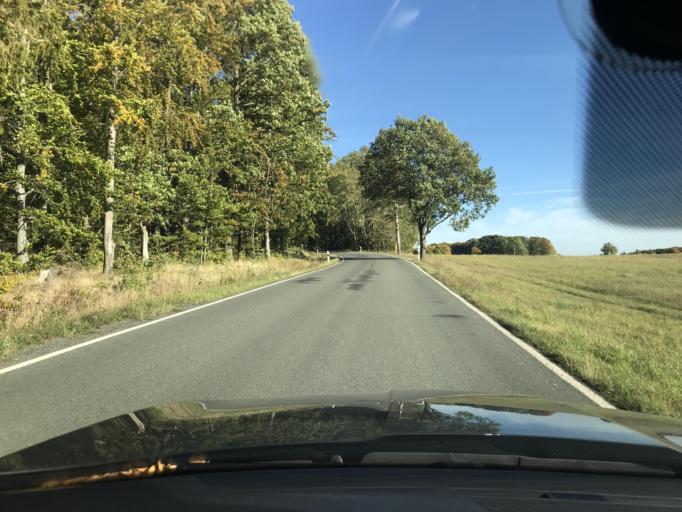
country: DE
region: Saxony-Anhalt
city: Friedrichsbrunn
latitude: 51.6827
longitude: 11.0135
